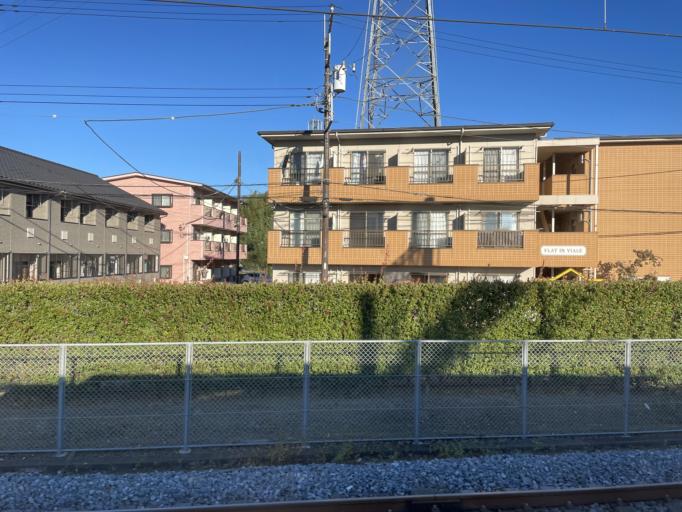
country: JP
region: Tochigi
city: Fujioka
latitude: 36.2238
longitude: 139.6483
